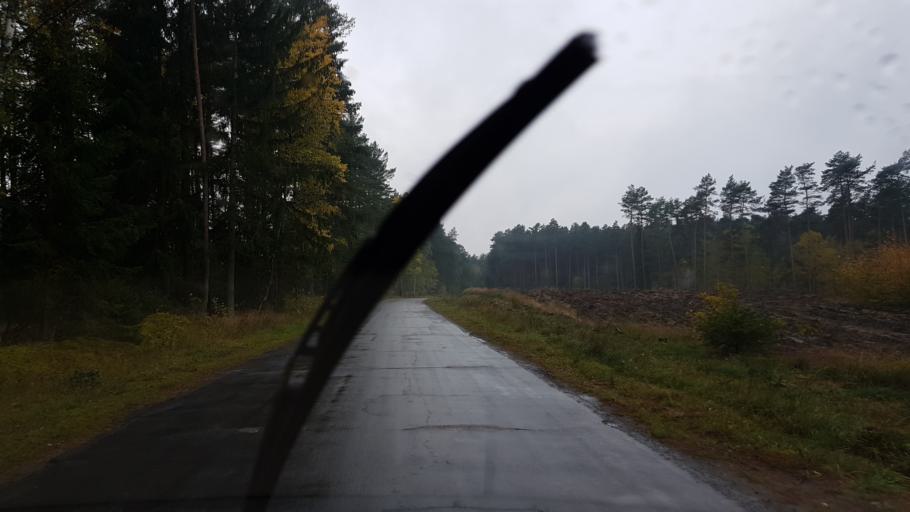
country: PL
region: West Pomeranian Voivodeship
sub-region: Powiat walecki
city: Walcz
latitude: 53.3787
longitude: 16.4706
